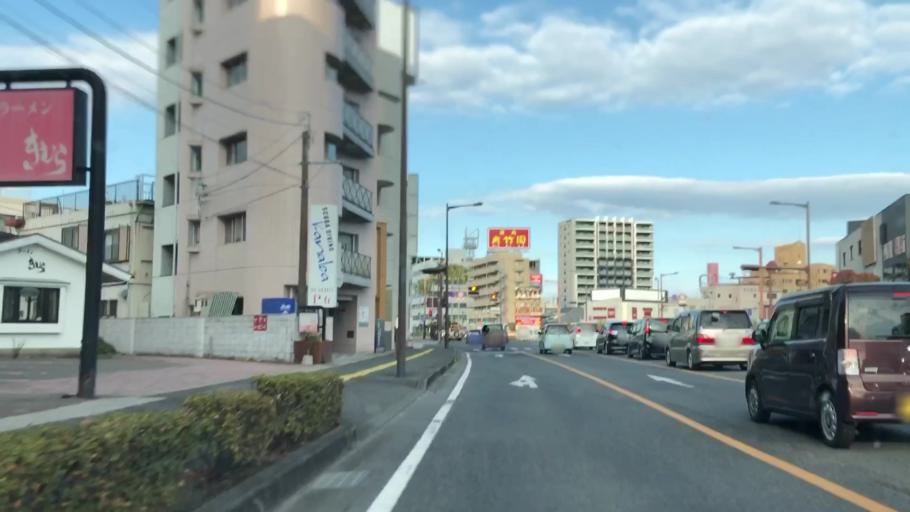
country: JP
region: Miyazaki
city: Miyazaki-shi
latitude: 31.8924
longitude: 131.4155
